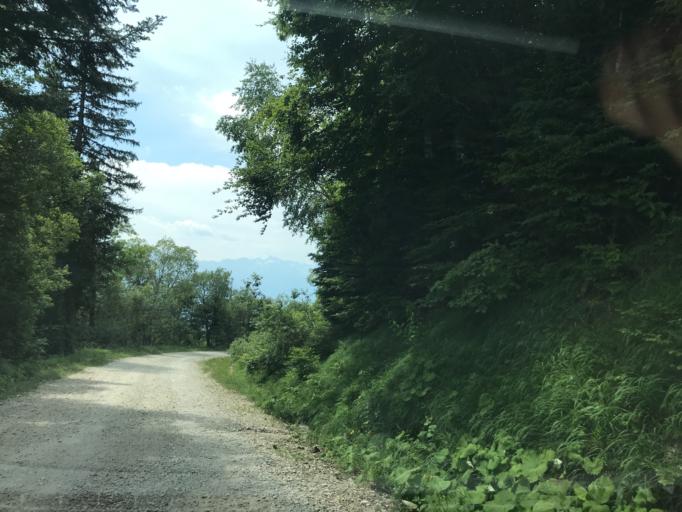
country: FR
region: Rhone-Alpes
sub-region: Departement de l'Isere
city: Barraux
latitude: 45.4186
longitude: 5.9372
